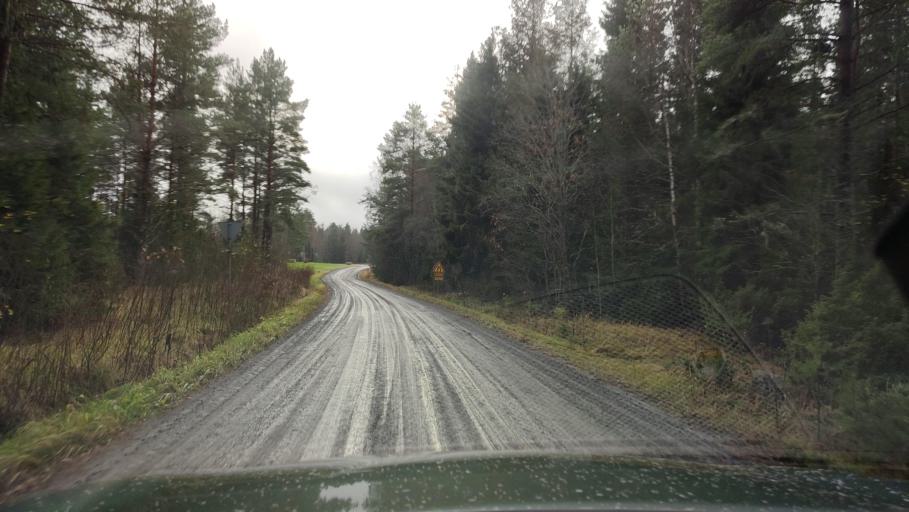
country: FI
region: Ostrobothnia
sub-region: Sydosterbotten
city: Naerpes
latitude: 62.4650
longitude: 21.4902
